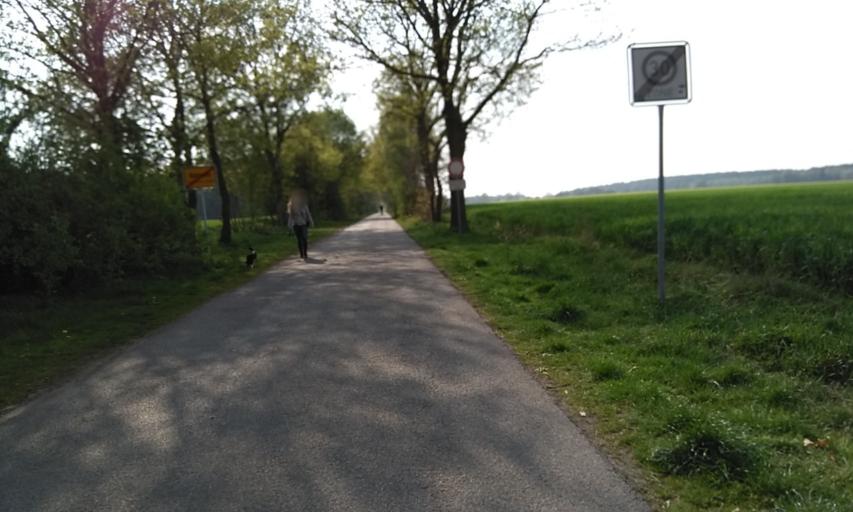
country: DE
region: Lower Saxony
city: Apensen
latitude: 53.4347
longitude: 9.6041
